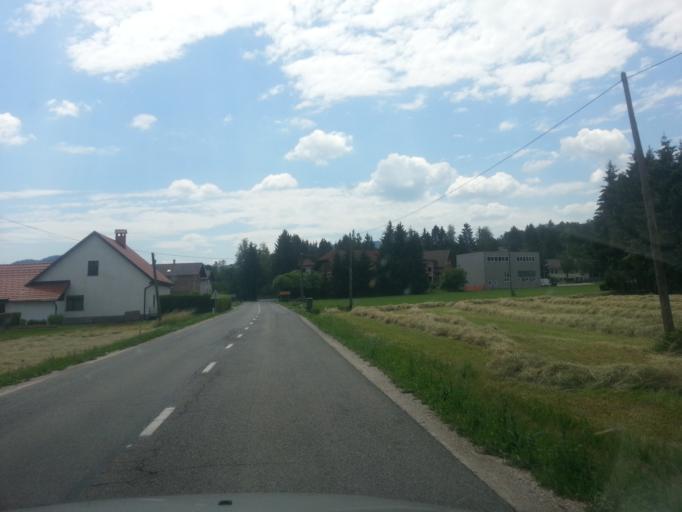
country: SI
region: Vrhnika
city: Vrhnika
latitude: 45.9760
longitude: 14.2908
